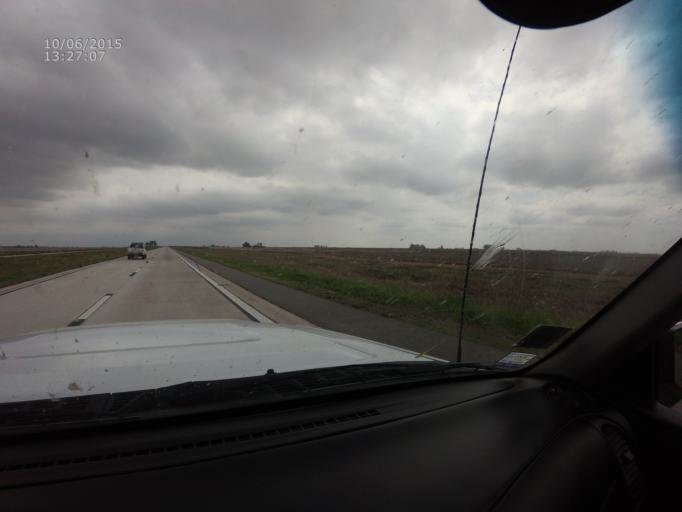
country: AR
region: Cordoba
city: Leones
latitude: -32.6469
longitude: -62.1959
